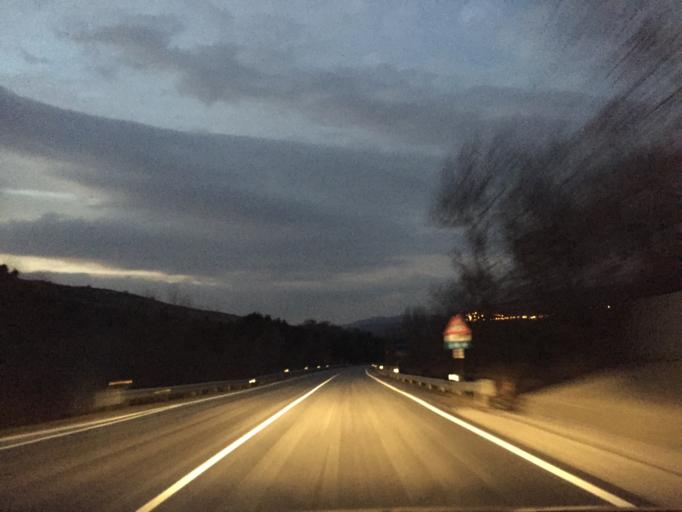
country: IT
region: Apulia
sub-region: Provincia di Foggia
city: Volturara Appula
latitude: 41.4698
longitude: 15.0553
